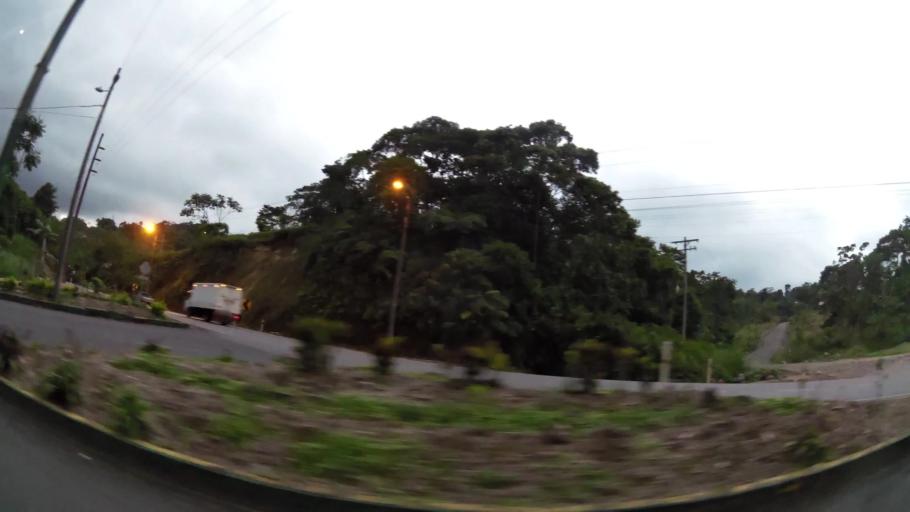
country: EC
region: Pastaza
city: Puyo
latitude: -1.4821
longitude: -78.0110
